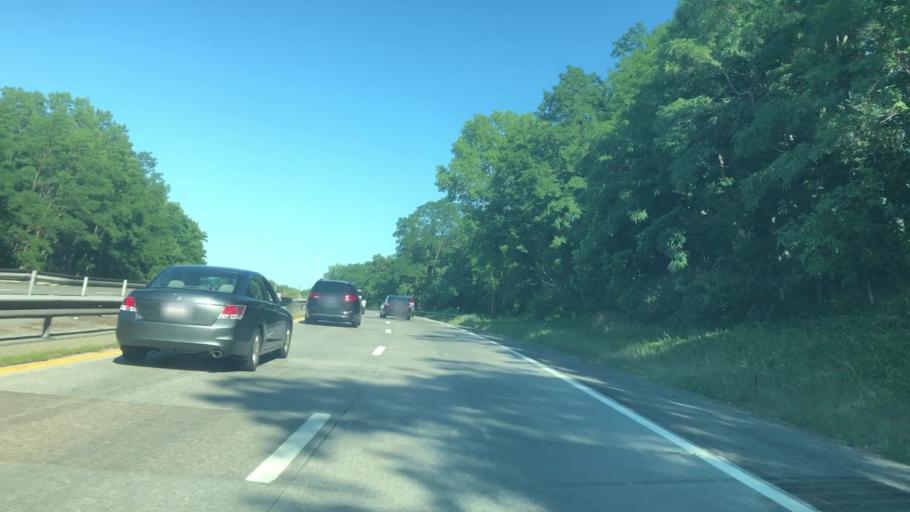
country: US
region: New York
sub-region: Monroe County
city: East Rochester
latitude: 43.1235
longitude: -77.5154
